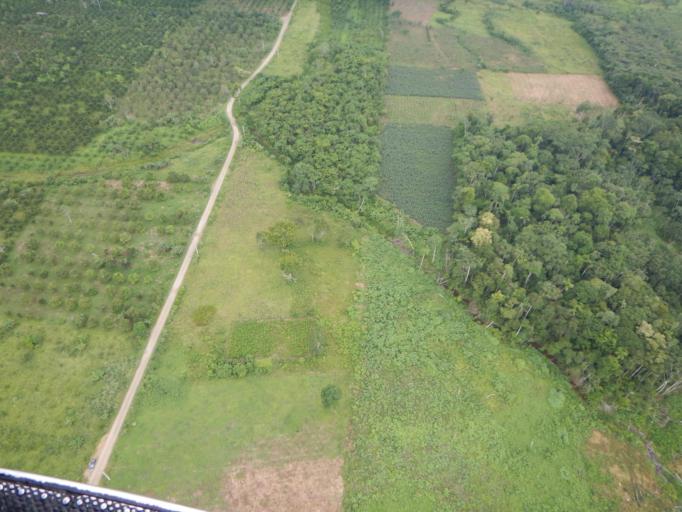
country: BO
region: Cochabamba
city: Chimore
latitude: -17.1250
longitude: -64.7956
